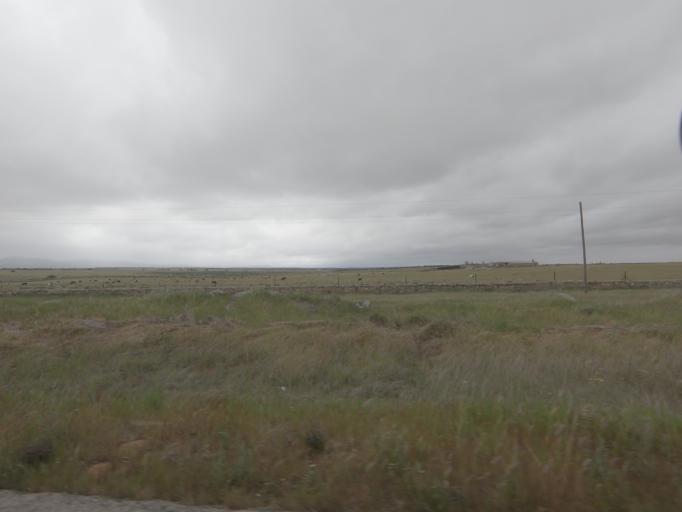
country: ES
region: Extremadura
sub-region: Provincia de Caceres
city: Malpartida de Caceres
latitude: 39.3742
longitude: -6.4529
